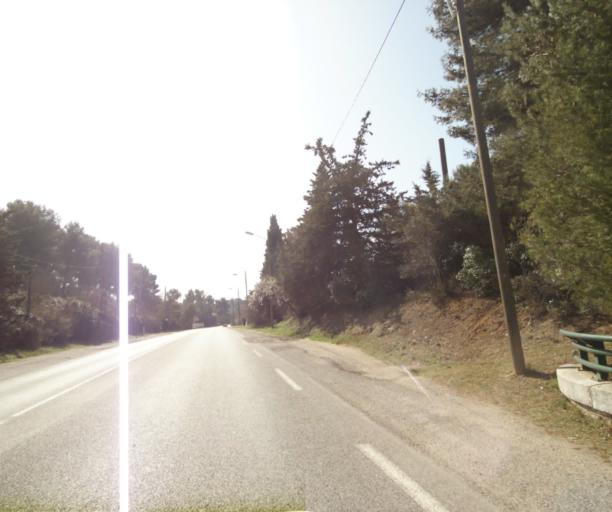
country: FR
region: Provence-Alpes-Cote d'Azur
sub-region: Departement des Bouches-du-Rhone
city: Aix-en-Provence
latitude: 43.4969
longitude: 5.4336
